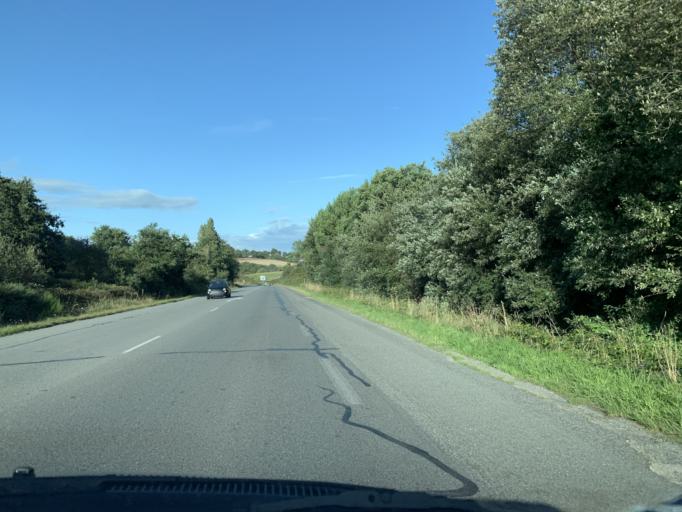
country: FR
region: Brittany
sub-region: Departement du Morbihan
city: Nivillac
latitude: 47.5091
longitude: -2.2906
